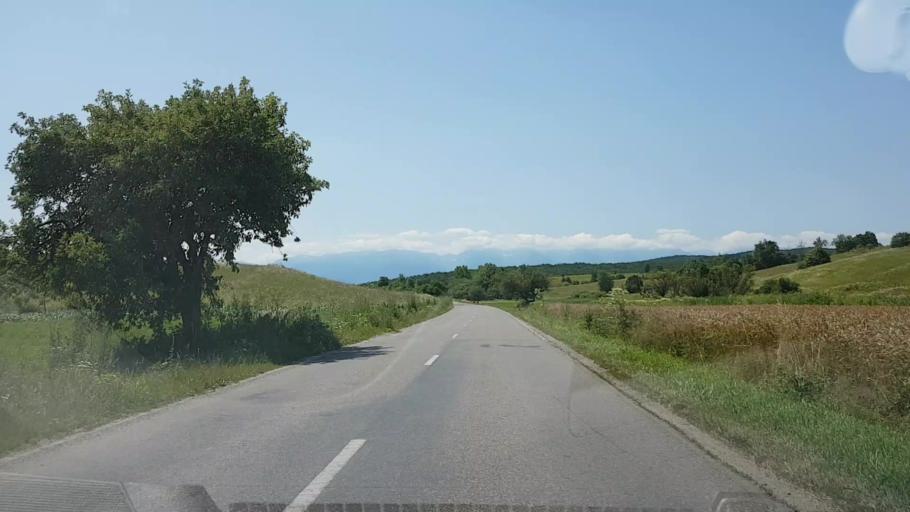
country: RO
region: Brasov
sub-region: Comuna Cincu
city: Cincu
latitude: 45.8959
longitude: 24.8119
